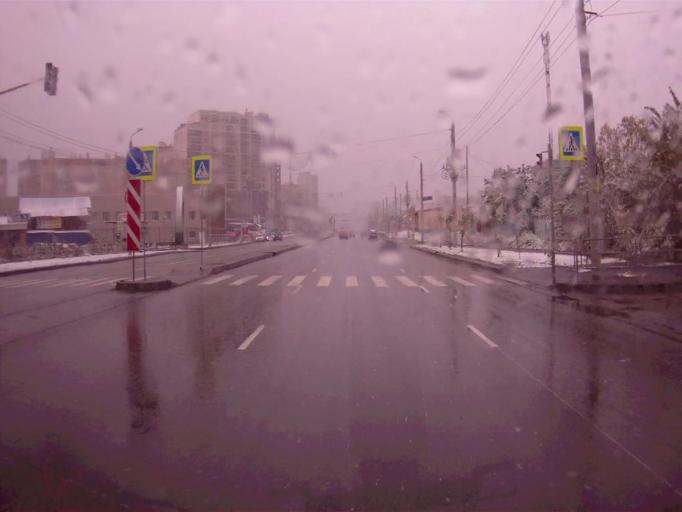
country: RU
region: Chelyabinsk
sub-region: Gorod Chelyabinsk
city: Chelyabinsk
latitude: 55.1443
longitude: 61.4042
